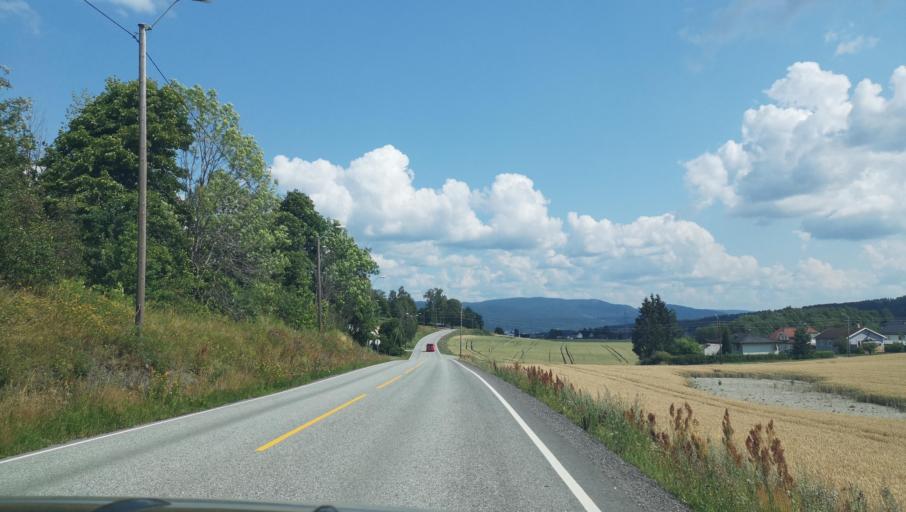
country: NO
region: Buskerud
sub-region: Ovre Eiker
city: Hokksund
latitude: 59.7373
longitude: 9.8555
